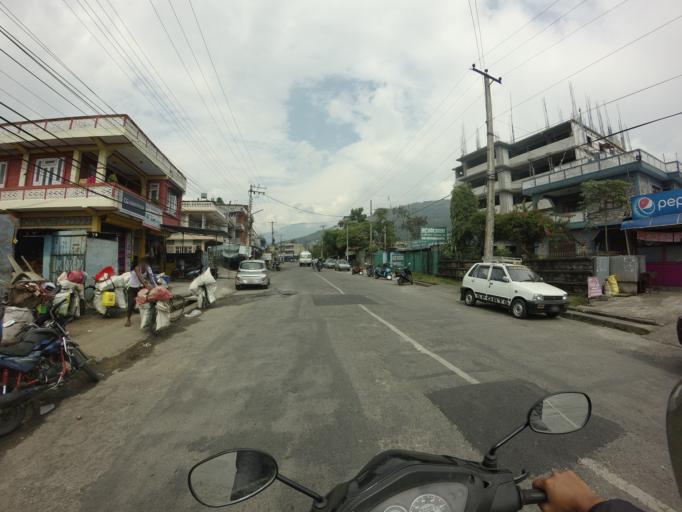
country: NP
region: Western Region
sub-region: Gandaki Zone
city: Pokhara
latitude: 28.2188
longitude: 83.9976
